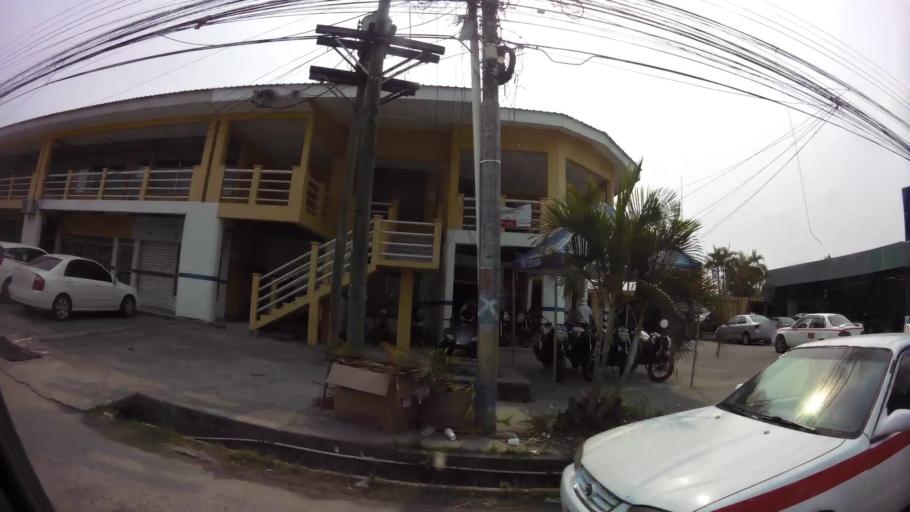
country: HN
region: Atlantida
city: Tela
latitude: 15.7795
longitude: -87.4518
